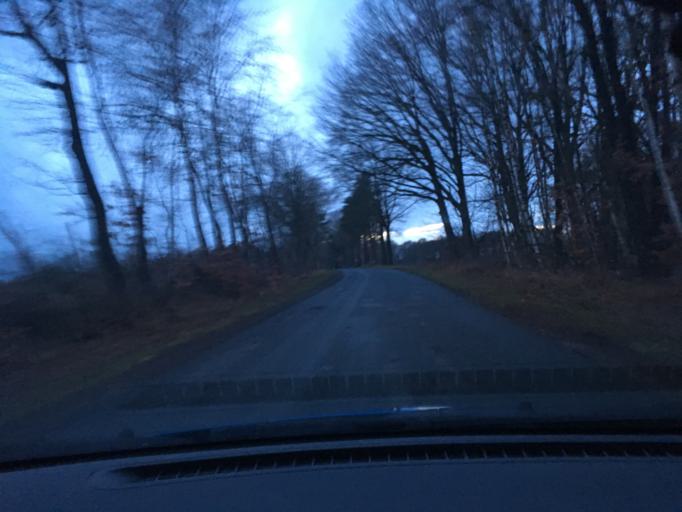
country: DE
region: Lower Saxony
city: Betzendorf
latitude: 53.1363
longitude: 10.3322
